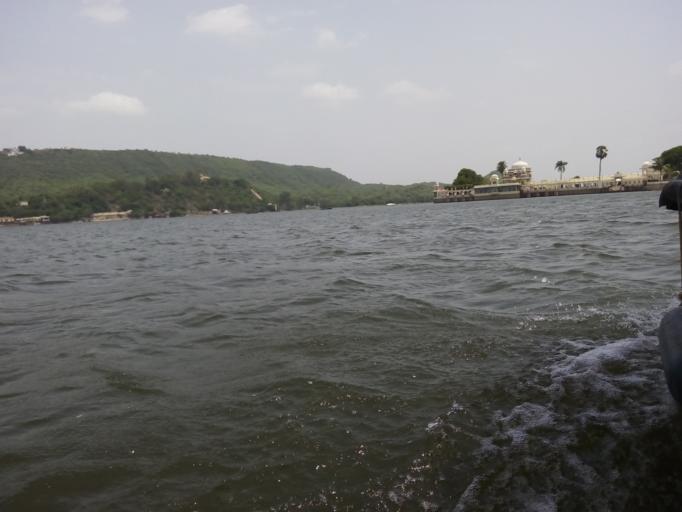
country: IN
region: Rajasthan
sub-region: Udaipur
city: Udaipur
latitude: 24.5703
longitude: 73.6776
